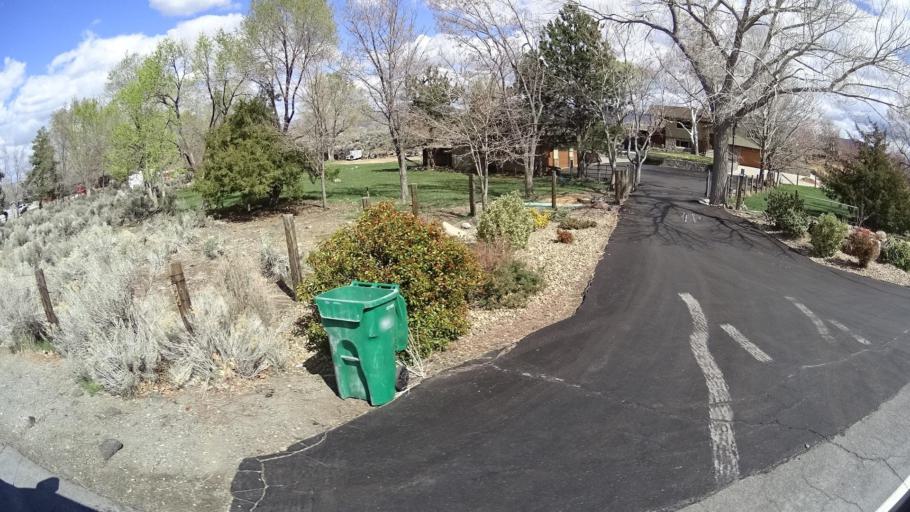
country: US
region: Nevada
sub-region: Washoe County
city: Reno
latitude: 39.4288
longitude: -119.7864
